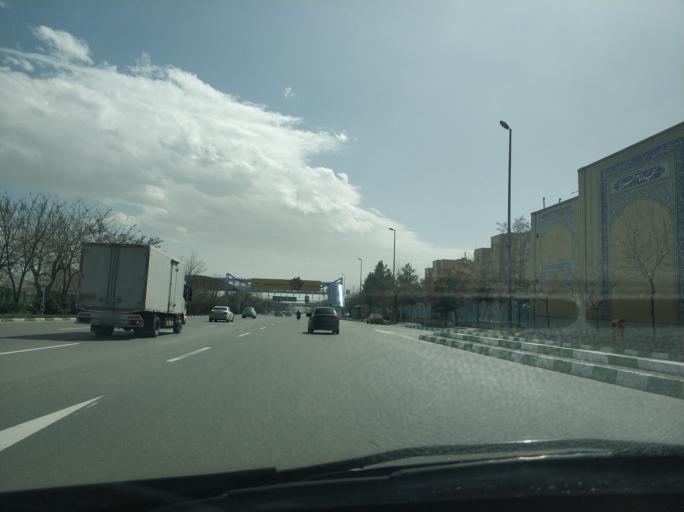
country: IR
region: Razavi Khorasan
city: Torqabeh
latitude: 36.3413
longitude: 59.4560
